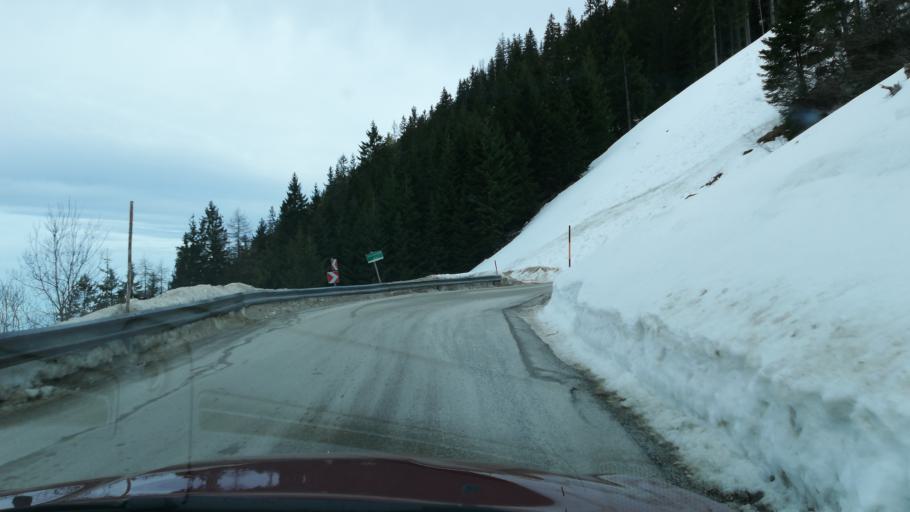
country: AT
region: Styria
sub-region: Politischer Bezirk Liezen
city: Donnersbach
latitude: 47.4116
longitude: 14.1837
